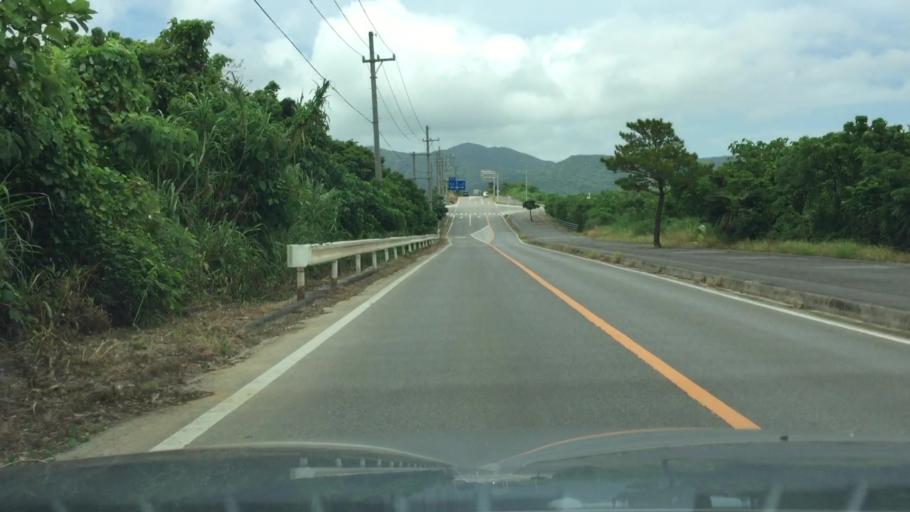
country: JP
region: Okinawa
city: Ishigaki
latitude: 24.4088
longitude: 124.2133
